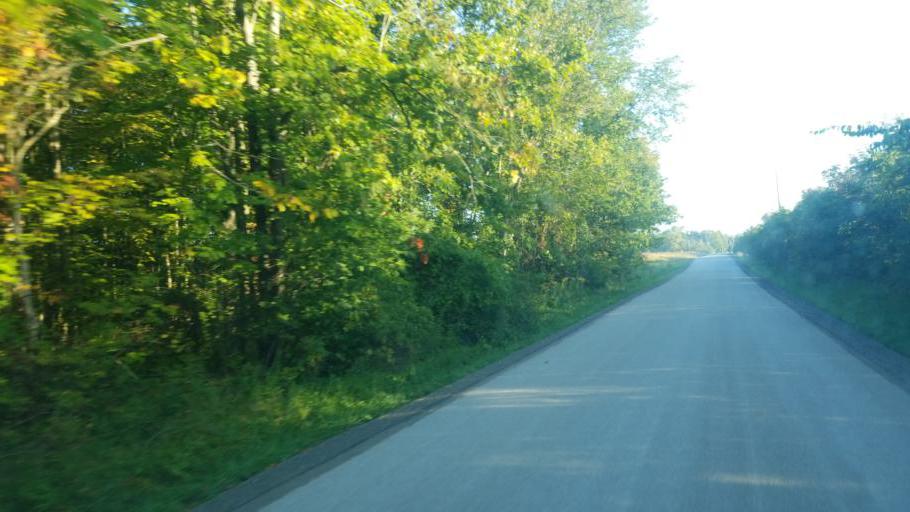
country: US
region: Ohio
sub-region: Lorain County
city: Wellington
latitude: 41.0654
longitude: -82.2582
